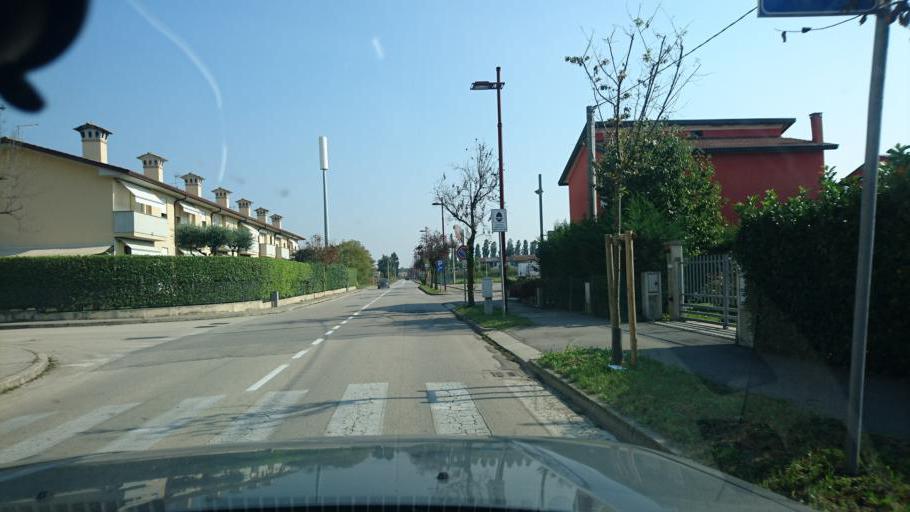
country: IT
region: Veneto
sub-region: Provincia di Padova
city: Bosco
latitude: 45.4426
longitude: 11.7985
